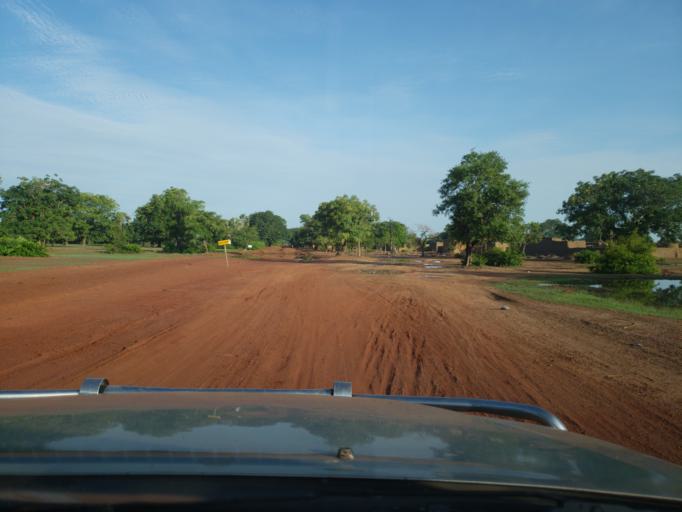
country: ML
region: Sikasso
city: Koutiala
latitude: 12.4207
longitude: -5.5825
